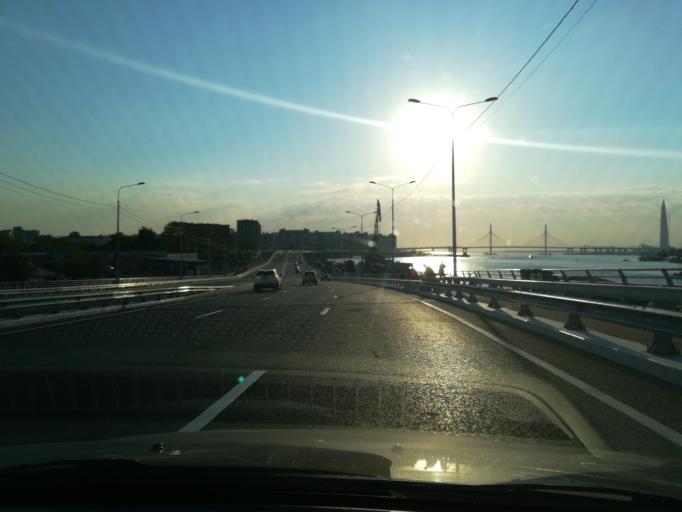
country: RU
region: Leningrad
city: Krestovskiy ostrov
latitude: 59.9579
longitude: 30.2535
